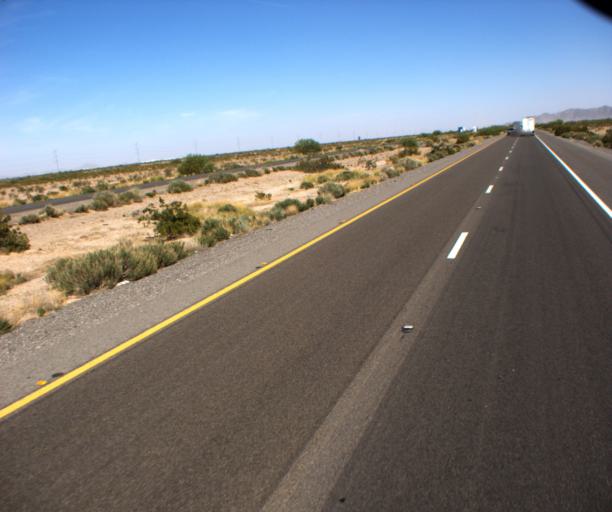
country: US
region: Arizona
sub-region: Pinal County
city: Casa Grande
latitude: 32.8279
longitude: -111.8506
